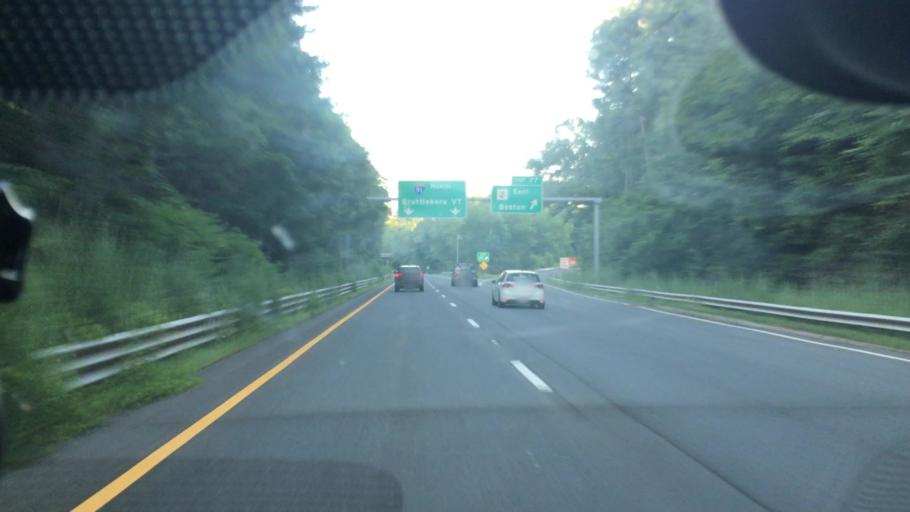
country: US
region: Massachusetts
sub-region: Franklin County
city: Greenfield
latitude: 42.6138
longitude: -72.5981
